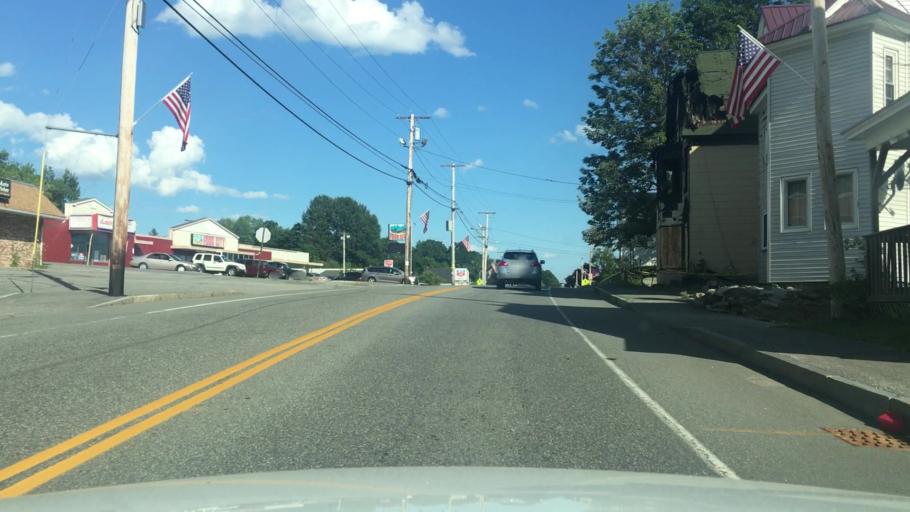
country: US
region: Maine
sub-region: Androscoggin County
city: Livermore Falls
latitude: 44.4769
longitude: -70.1944
